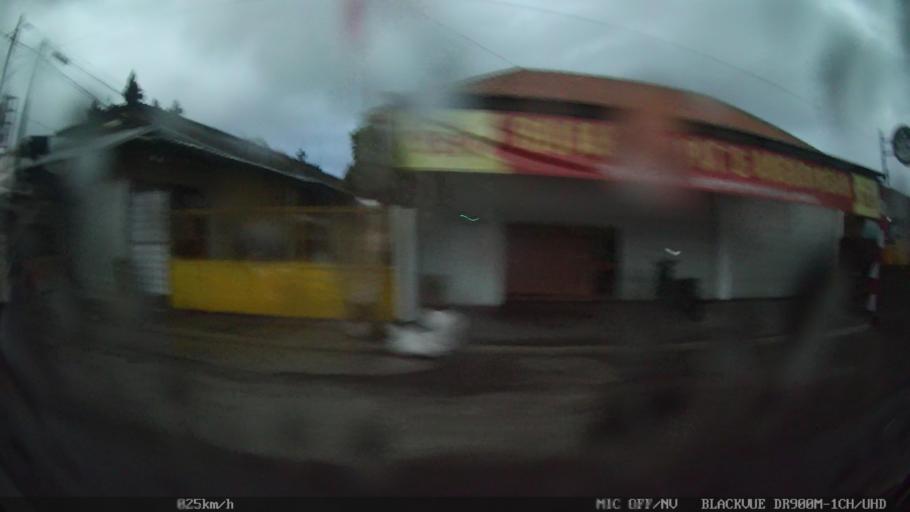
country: ID
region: Bali
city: Banjar Kayangan
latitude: -8.6147
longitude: 115.2221
